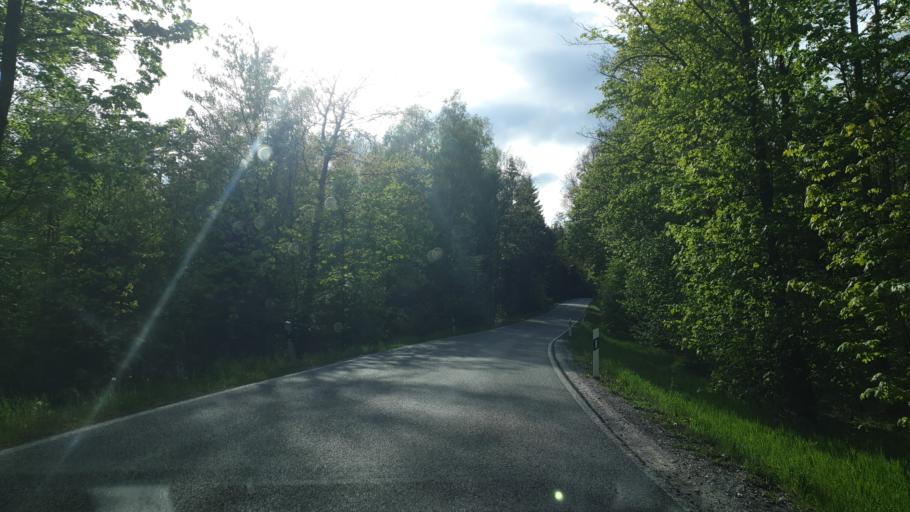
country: DE
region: Saxony
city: Hohndorf
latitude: 50.7174
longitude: 12.6573
